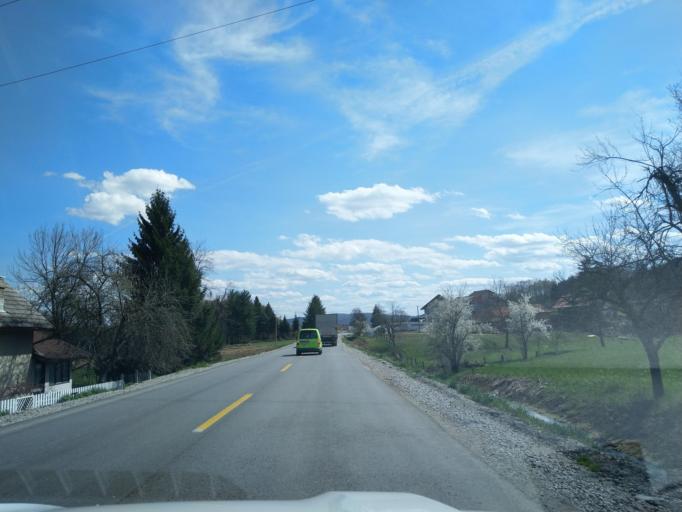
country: RS
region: Central Serbia
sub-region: Zlatiborski Okrug
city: Pozega
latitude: 43.8207
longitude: 20.0845
